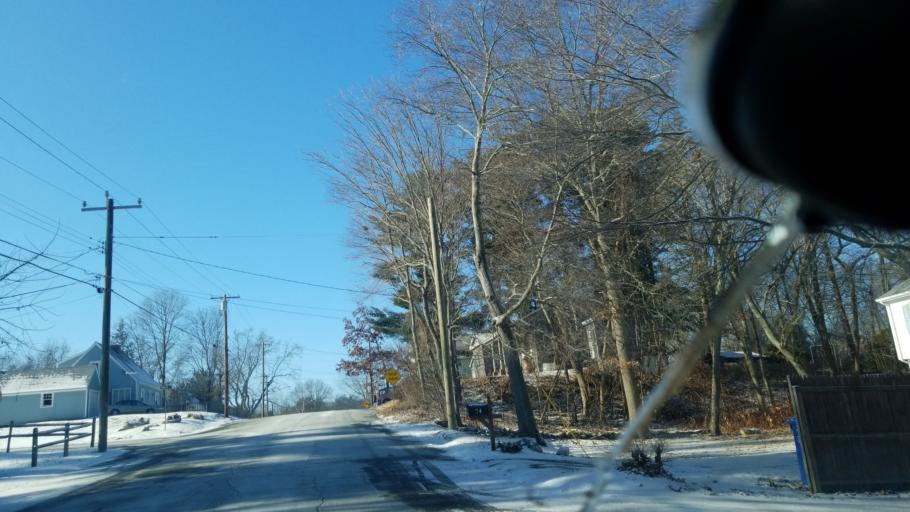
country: US
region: Connecticut
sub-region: Windham County
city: Danielson
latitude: 41.8209
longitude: -71.8815
